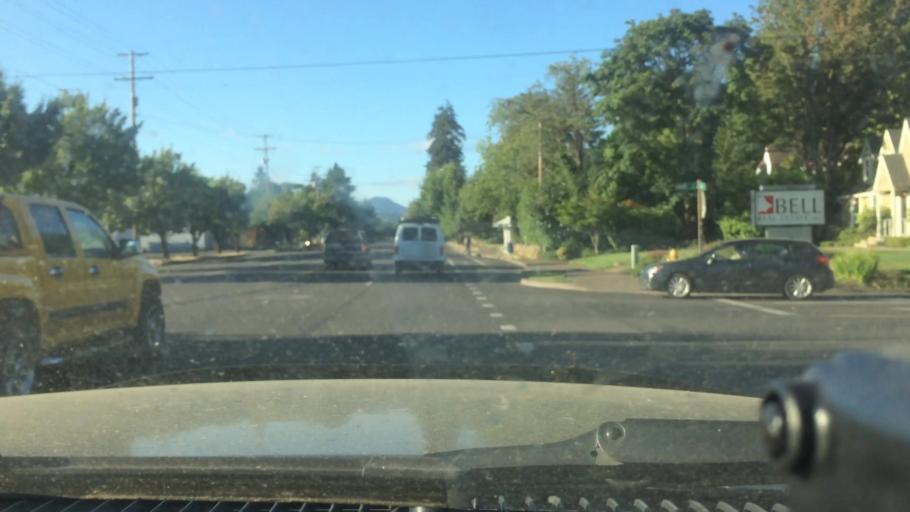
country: US
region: Oregon
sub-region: Lane County
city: Eugene
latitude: 44.0717
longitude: -123.1187
